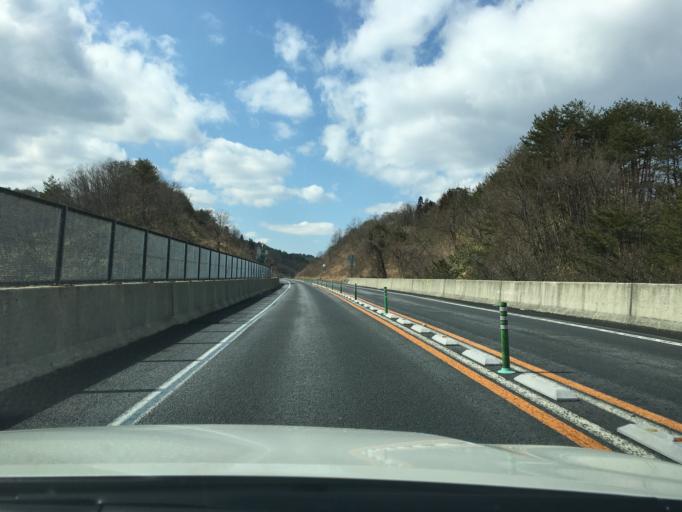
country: JP
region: Yamagata
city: Sagae
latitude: 38.4020
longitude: 140.2039
